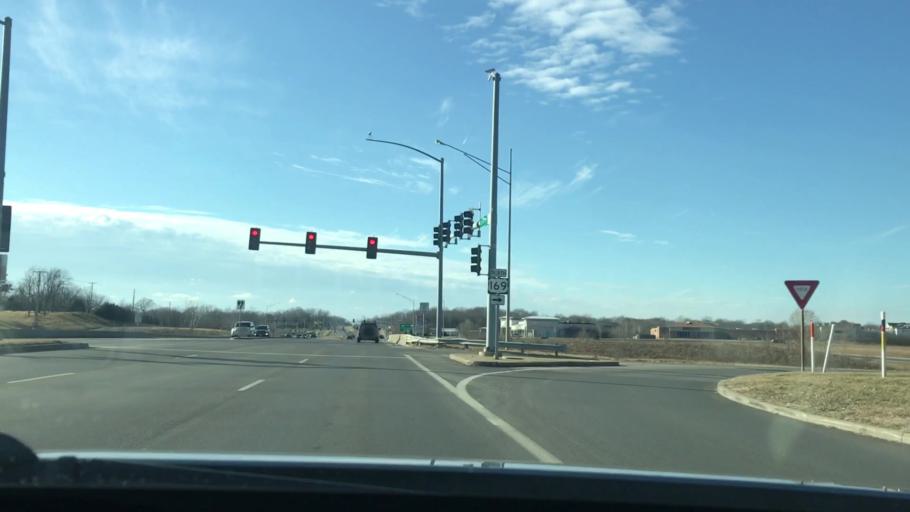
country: US
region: Missouri
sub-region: Clay County
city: Gladstone
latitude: 39.2465
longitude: -94.5893
